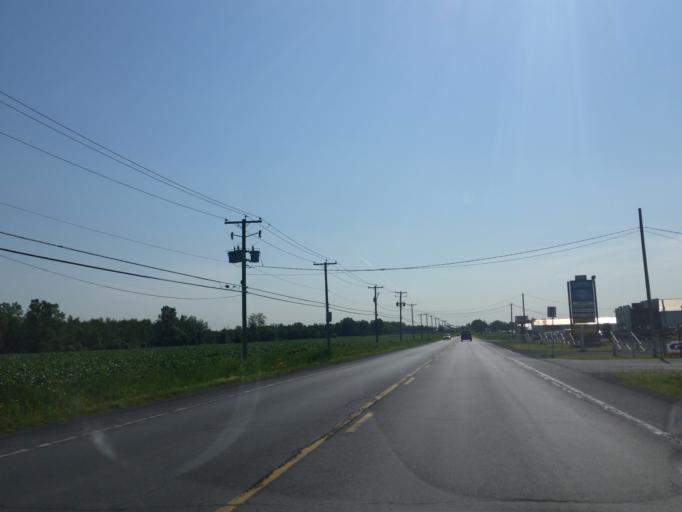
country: CA
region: Quebec
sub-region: Monteregie
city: Napierville
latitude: 45.1953
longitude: -73.4419
